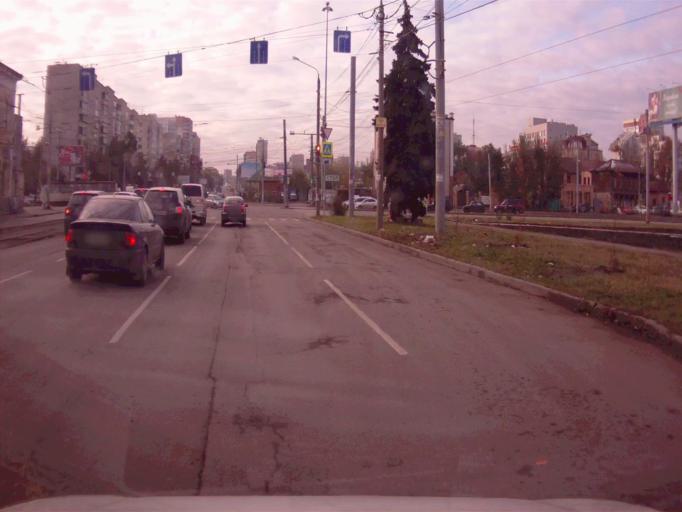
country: RU
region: Chelyabinsk
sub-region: Gorod Chelyabinsk
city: Chelyabinsk
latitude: 55.1690
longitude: 61.4155
